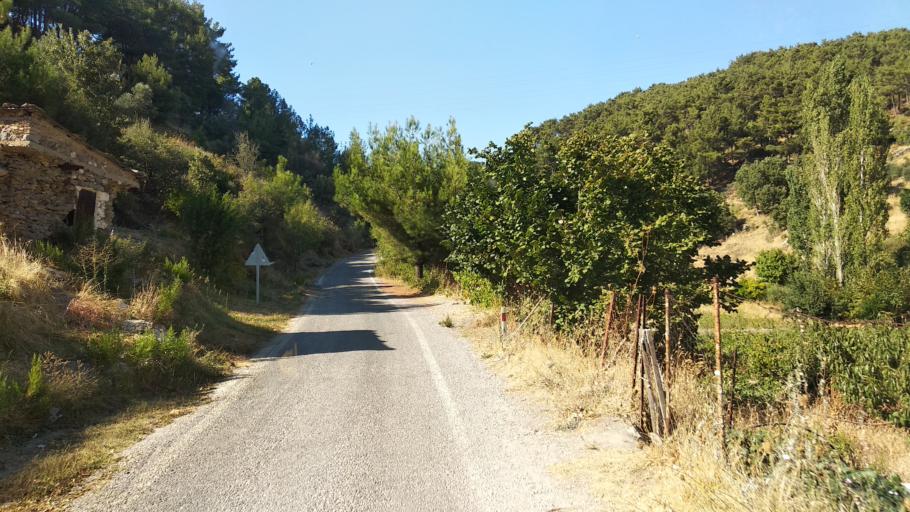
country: TR
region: Izmir
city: Gaziemir
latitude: 38.3249
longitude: 26.9570
